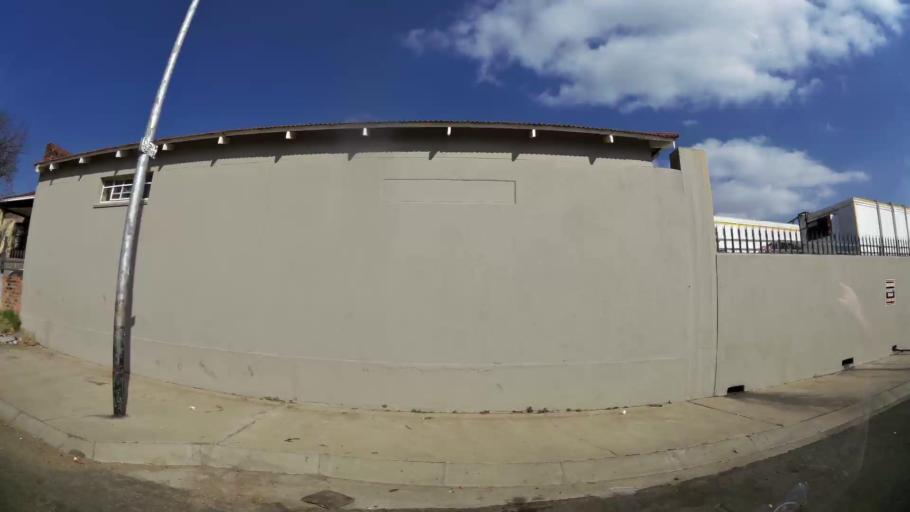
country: ZA
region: Gauteng
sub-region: West Rand District Municipality
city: Krugersdorp
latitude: -26.1086
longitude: 27.7766
